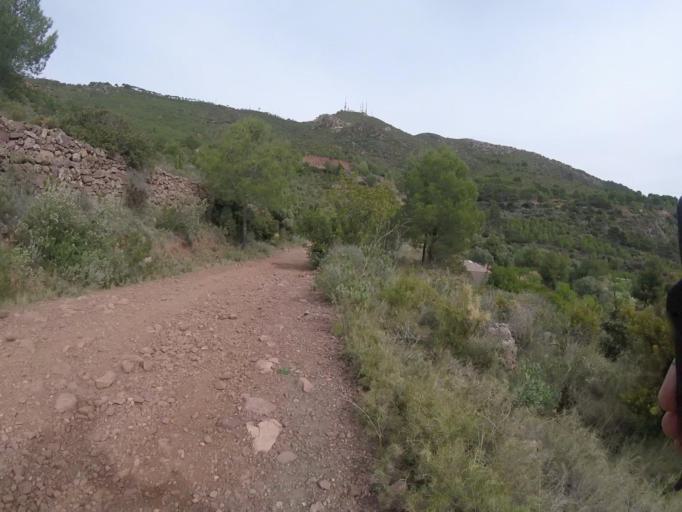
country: ES
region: Valencia
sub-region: Provincia de Castello
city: Benicassim
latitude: 40.0762
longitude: 0.0313
